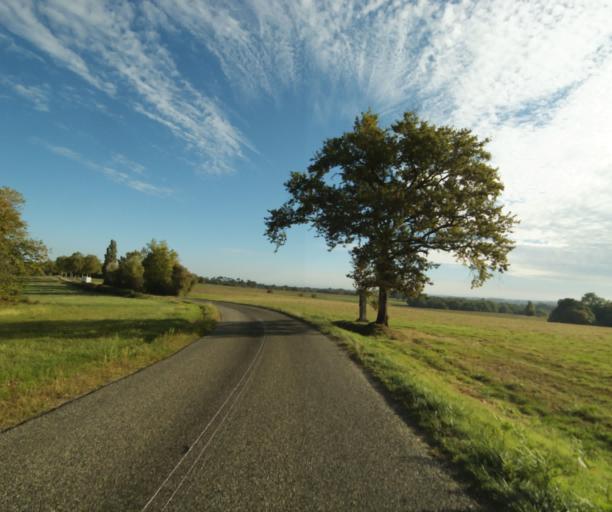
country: FR
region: Midi-Pyrenees
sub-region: Departement du Gers
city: Eauze
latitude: 43.8874
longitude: 0.0310
